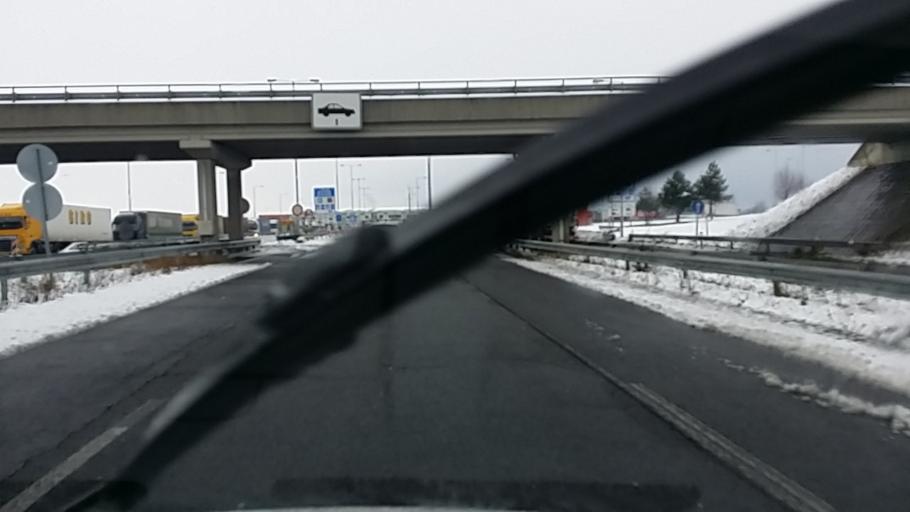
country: HU
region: Gyor-Moson-Sopron
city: Rajka
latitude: 48.0125
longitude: 17.1760
